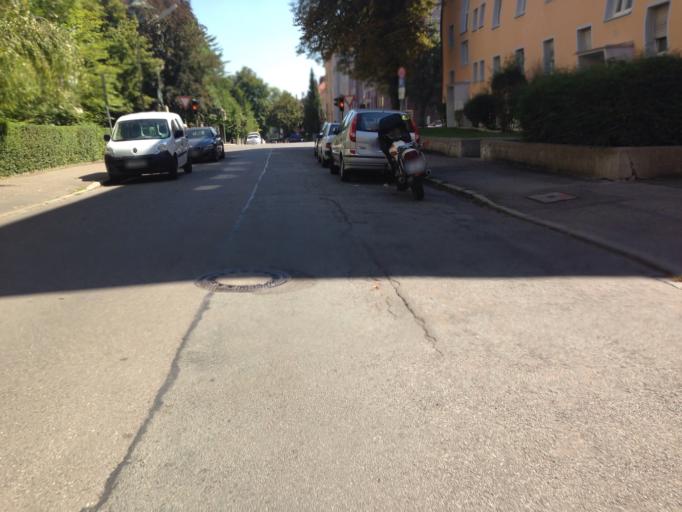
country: DE
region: Bavaria
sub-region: Swabia
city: Augsburg
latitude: 48.3582
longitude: 10.8990
